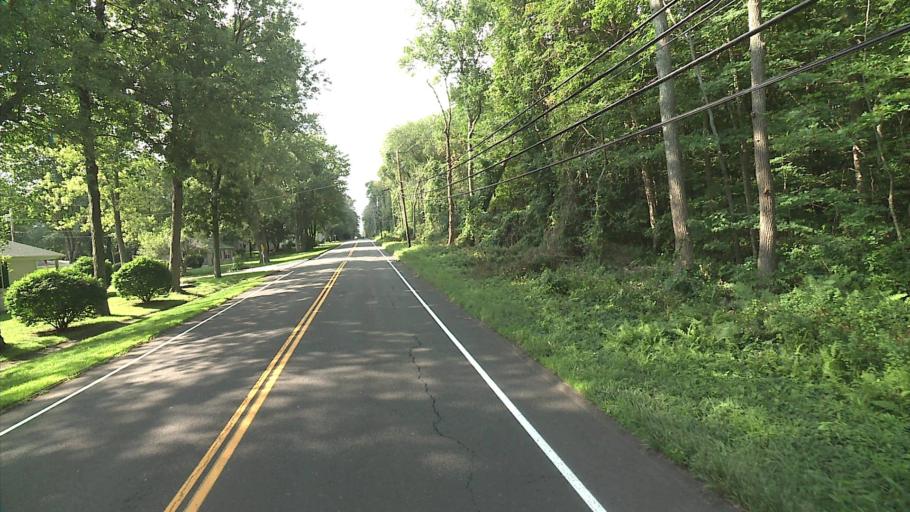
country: US
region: Connecticut
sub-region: New Haven County
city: Madison
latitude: 41.3792
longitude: -72.5663
